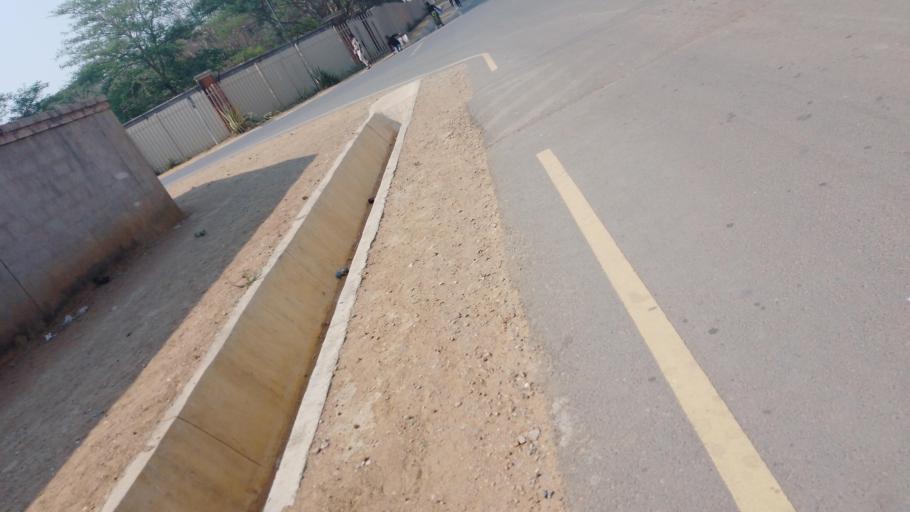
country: ZM
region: Lusaka
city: Lusaka
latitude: -15.3902
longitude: 28.3914
